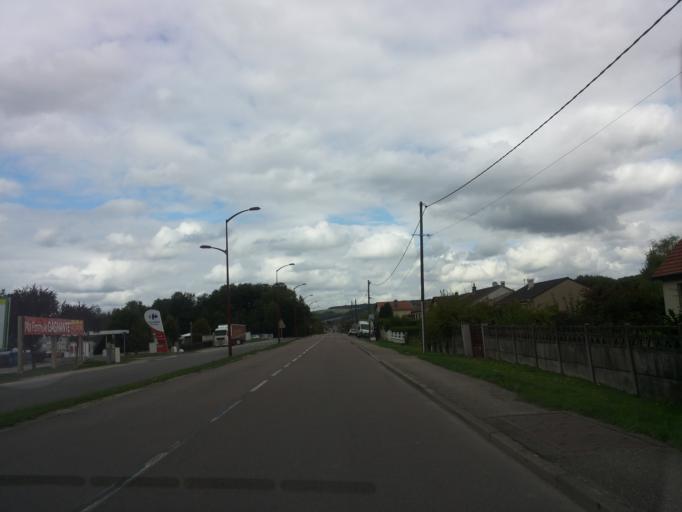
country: FR
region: Lorraine
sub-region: Departement de la Meuse
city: Ligny-en-Barrois
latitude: 48.6764
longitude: 5.3258
